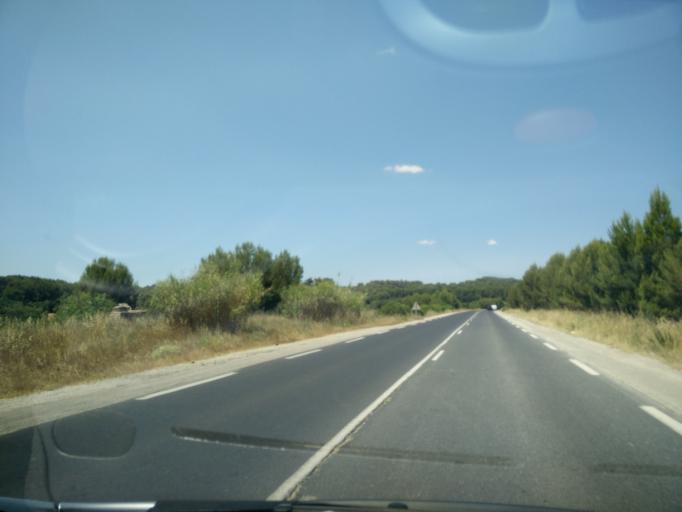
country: FR
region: Languedoc-Roussillon
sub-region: Departement de l'Herault
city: Villetelle
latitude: 43.7088
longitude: 4.1170
